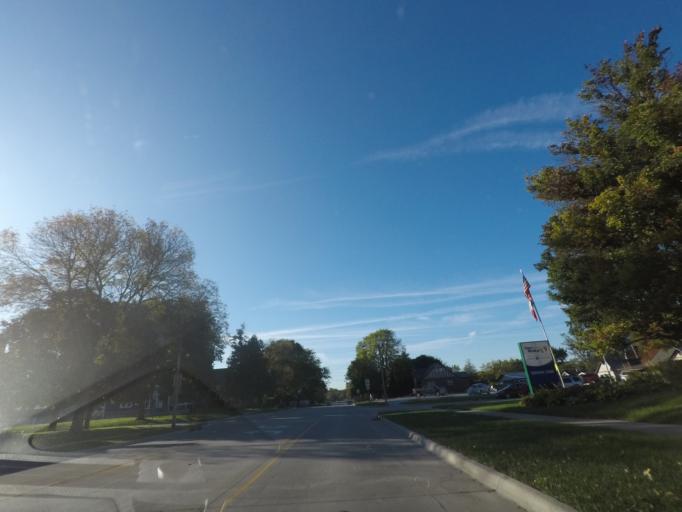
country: US
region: Iowa
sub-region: Story County
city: Nevada
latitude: 42.0169
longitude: -93.4523
